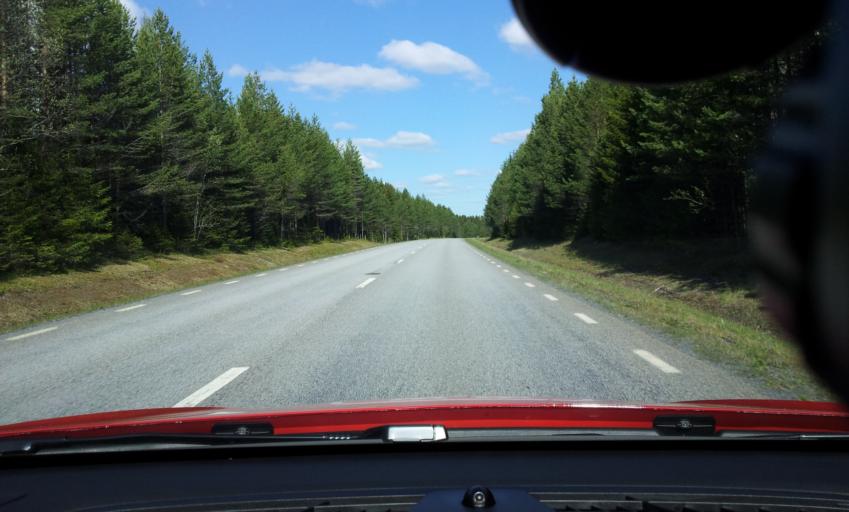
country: SE
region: Jaemtland
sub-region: Krokoms Kommun
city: Valla
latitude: 63.2714
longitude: 13.9515
